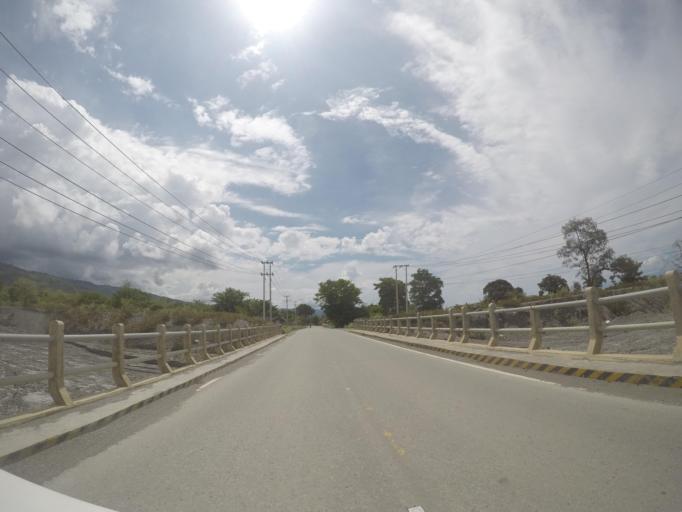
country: TL
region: Liquica
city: Liquica
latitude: -8.5847
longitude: 125.3531
